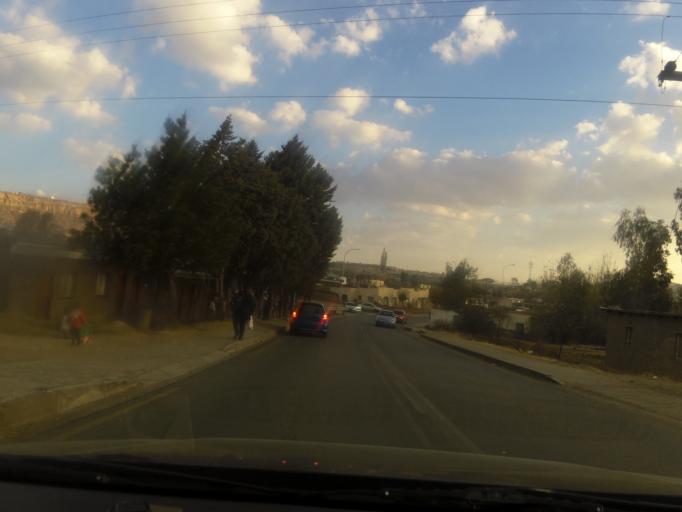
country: LS
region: Maseru
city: Maseru
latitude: -29.3074
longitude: 27.5310
